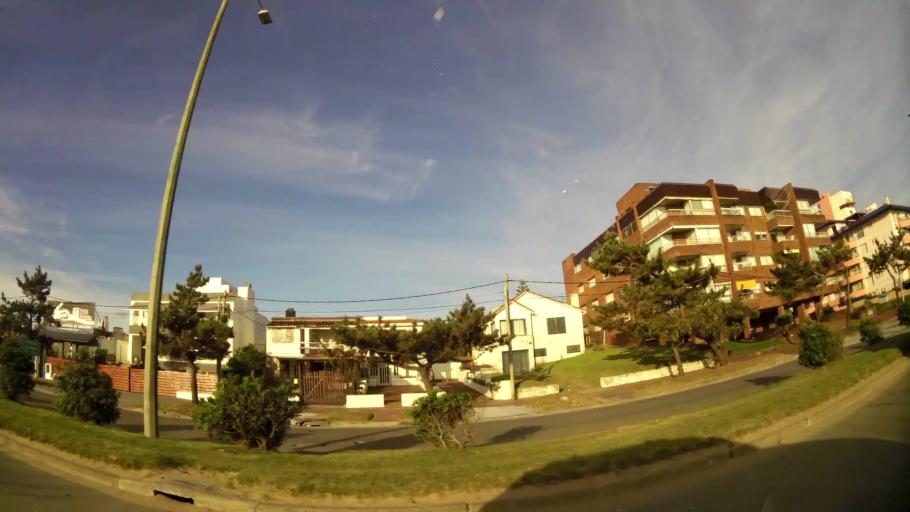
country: UY
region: Maldonado
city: Maldonado
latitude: -34.9216
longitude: -54.9693
